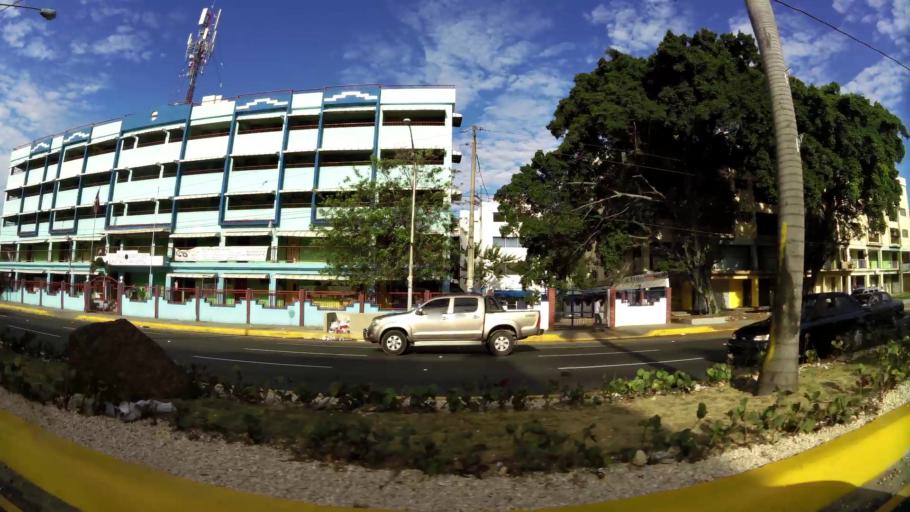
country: DO
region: Nacional
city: San Carlos
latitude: 18.4883
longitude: -69.9043
